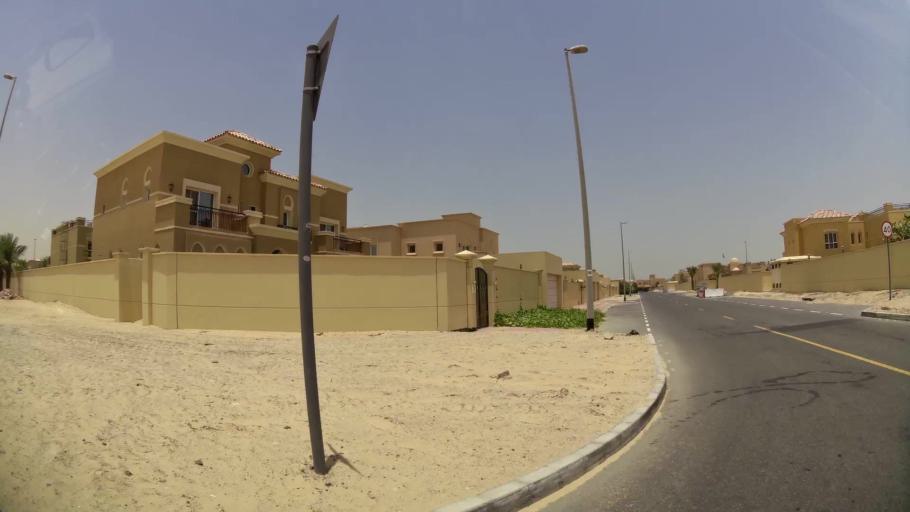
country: AE
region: Dubai
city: Dubai
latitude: 25.0879
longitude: 55.2385
